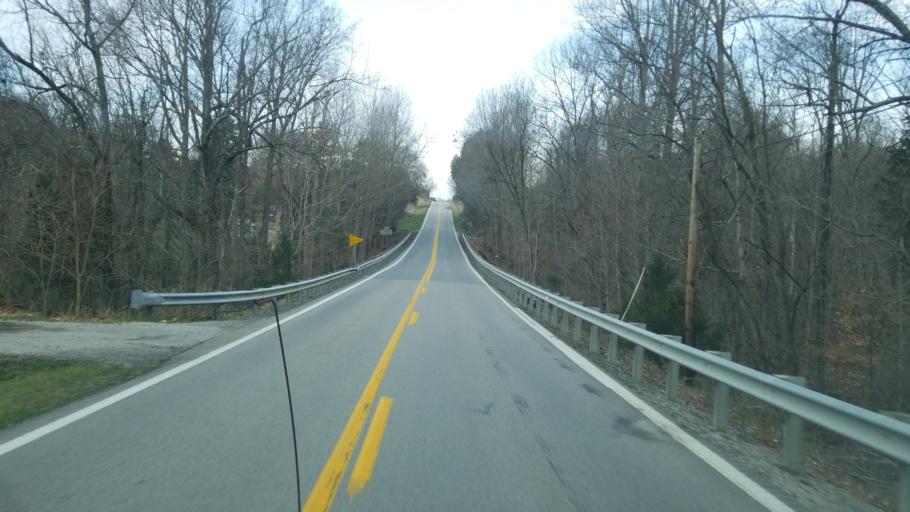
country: US
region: Kentucky
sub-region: Clinton County
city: Albany
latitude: 36.7564
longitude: -85.1503
